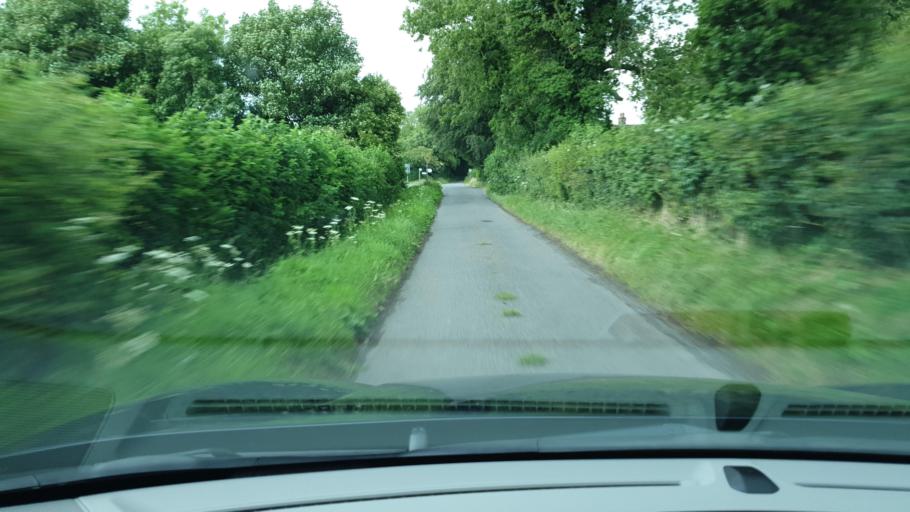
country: IE
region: Leinster
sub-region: An Mhi
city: Navan
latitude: 53.5908
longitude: -6.6240
